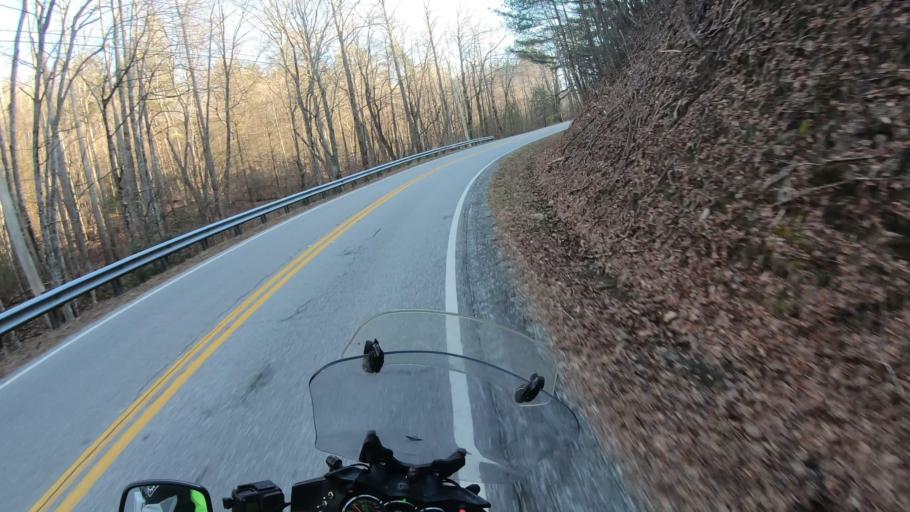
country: US
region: Georgia
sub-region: Union County
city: Blairsville
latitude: 34.7108
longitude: -84.0463
